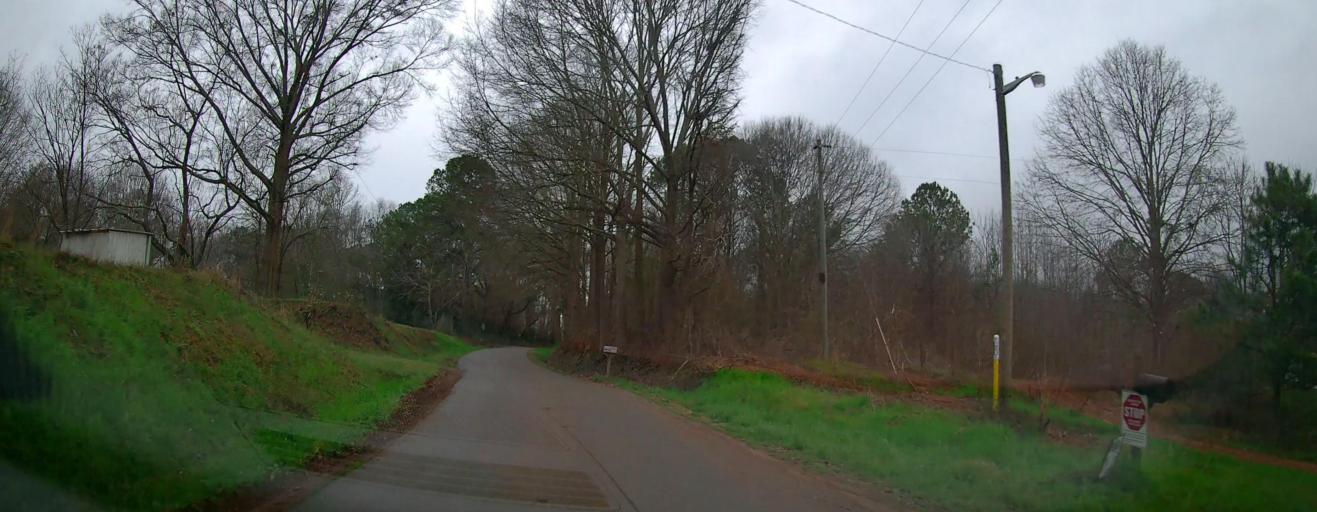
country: US
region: Georgia
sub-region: Monroe County
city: Forsyth
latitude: 33.0520
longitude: -83.8857
